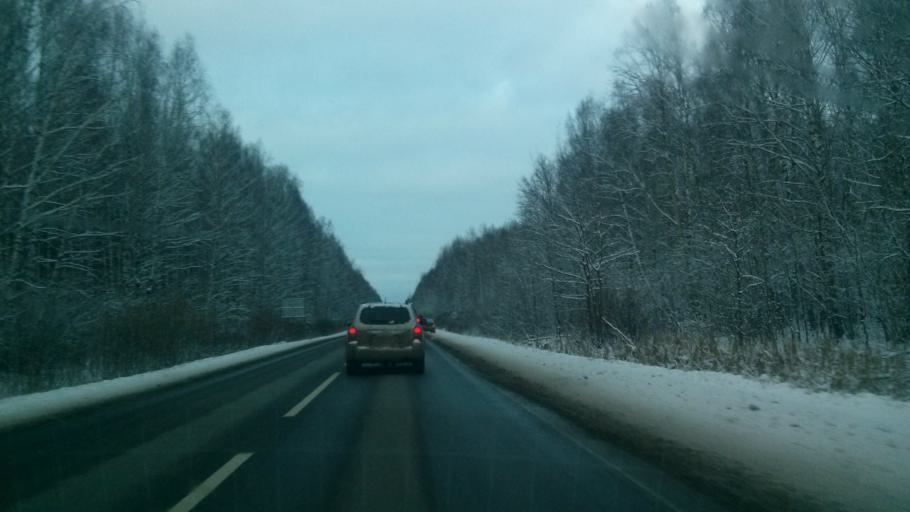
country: RU
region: Nizjnij Novgorod
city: Vorsma
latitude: 56.0135
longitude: 43.3438
